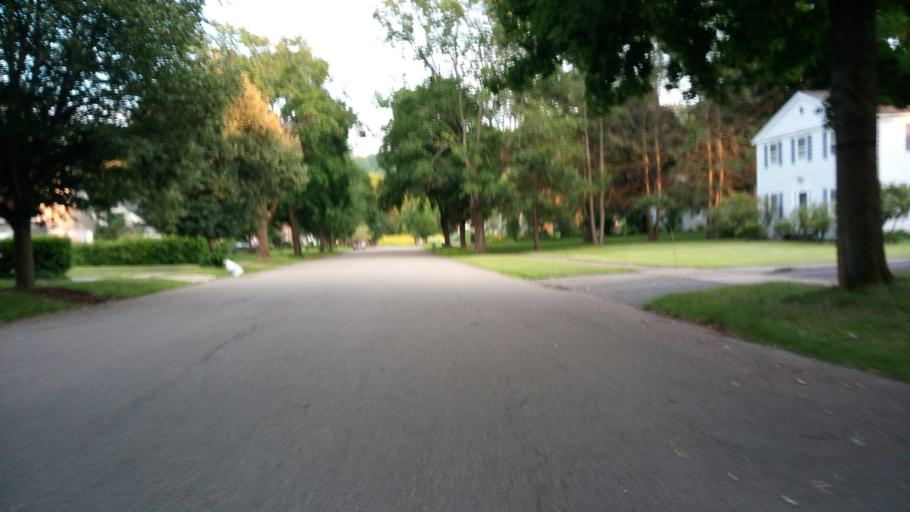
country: US
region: New York
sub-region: Chemung County
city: West Elmira
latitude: 42.0771
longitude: -76.8434
